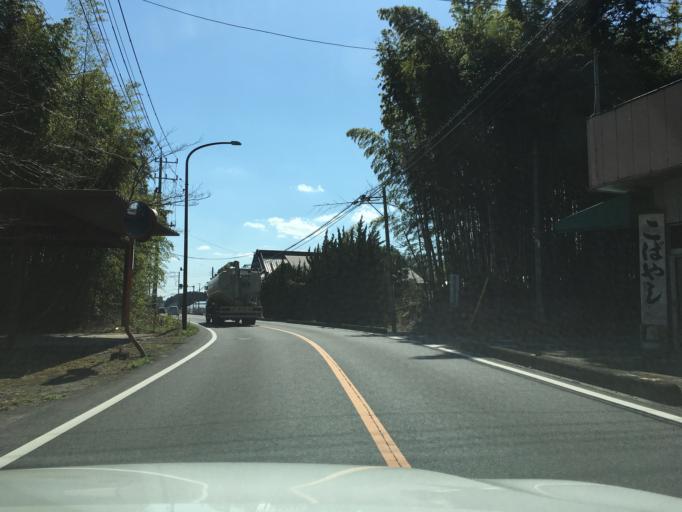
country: JP
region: Tochigi
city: Otawara
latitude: 36.8865
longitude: 140.1180
